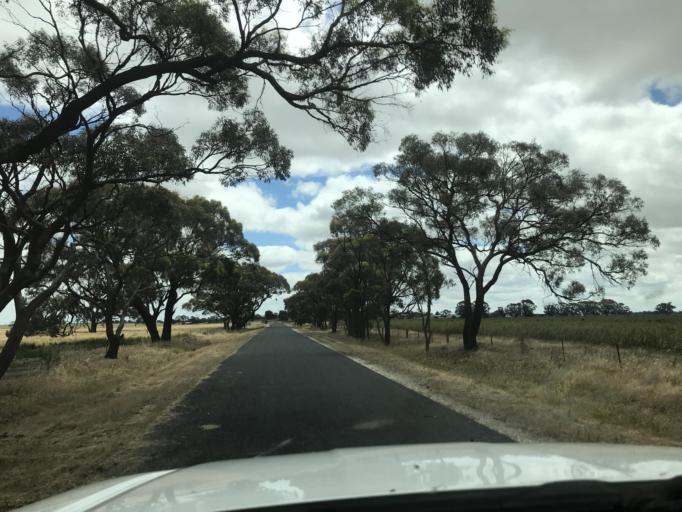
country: AU
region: South Australia
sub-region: Tatiara
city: Bordertown
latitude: -36.3571
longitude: 141.1950
